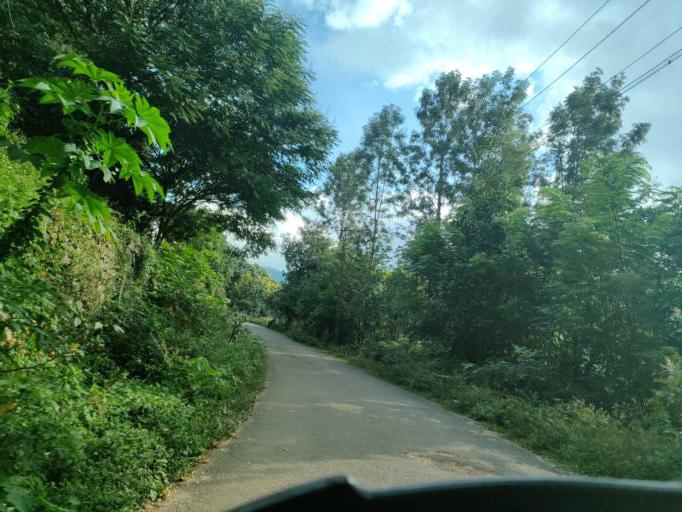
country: IN
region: Tamil Nadu
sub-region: Dindigul
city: Kodaikanal
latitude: 10.2804
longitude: 77.5293
